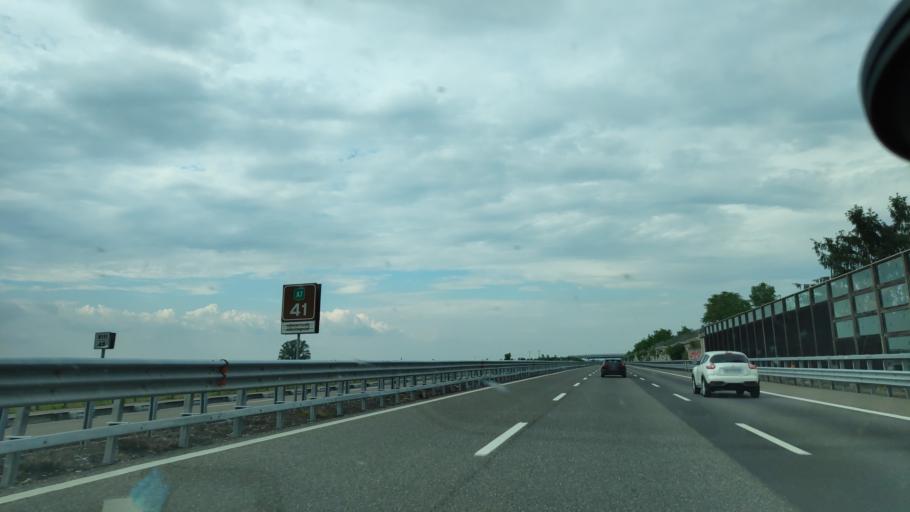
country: IT
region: Lombardy
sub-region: Provincia di Pavia
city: Silvano Pietra
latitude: 45.0396
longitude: 8.9415
